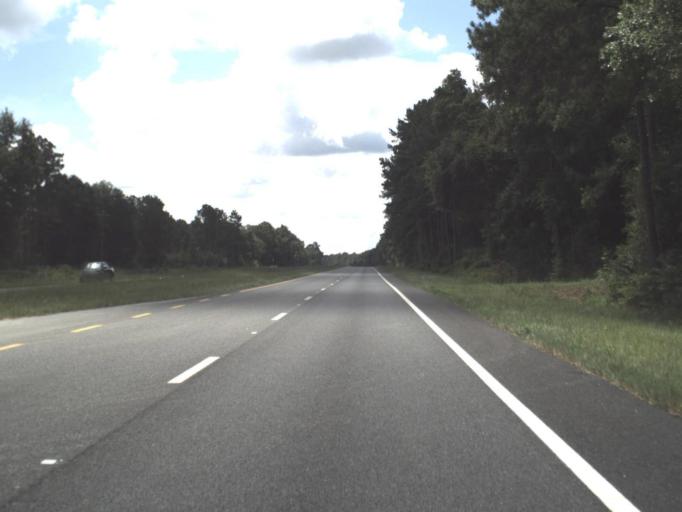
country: US
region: Florida
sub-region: Jefferson County
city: Monticello
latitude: 30.3448
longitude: -83.7895
